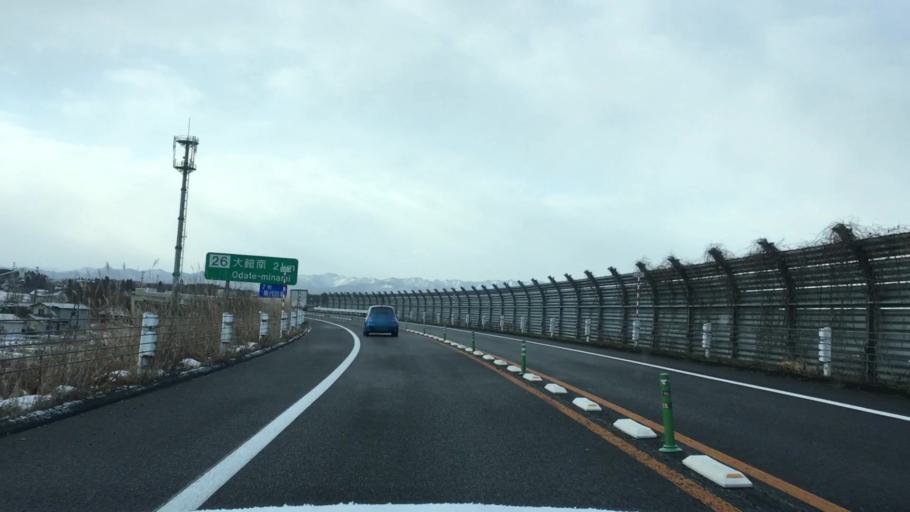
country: JP
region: Akita
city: Odate
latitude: 40.2876
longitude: 140.5420
